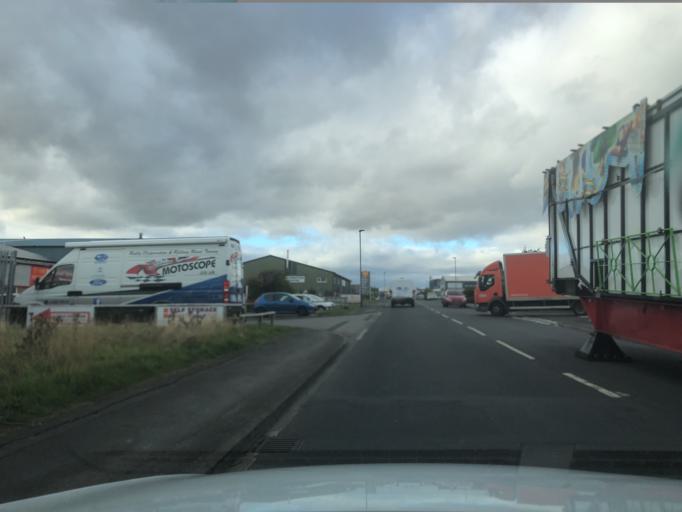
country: GB
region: England
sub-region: North Yorkshire
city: Northallerton
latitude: 54.3469
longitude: -1.4478
